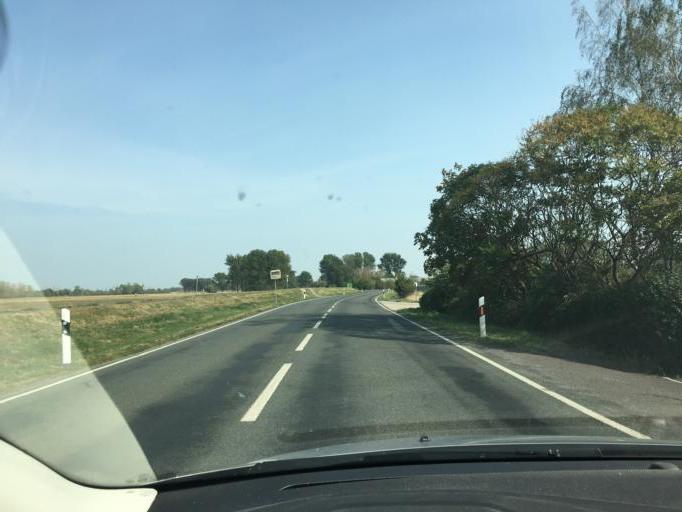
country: DE
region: Saxony-Anhalt
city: Plotzky
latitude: 52.0101
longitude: 11.7868
